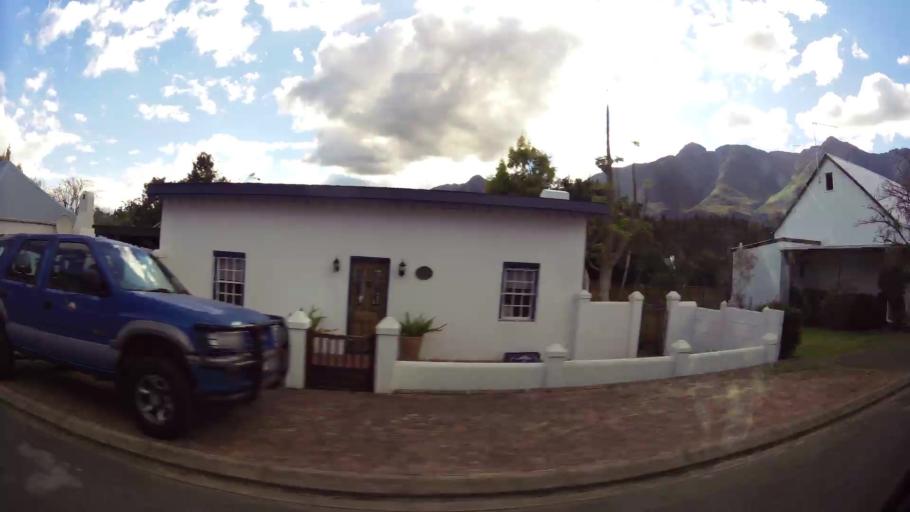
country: ZA
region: Western Cape
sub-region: Overberg District Municipality
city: Swellendam
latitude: -34.0155
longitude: 20.4543
